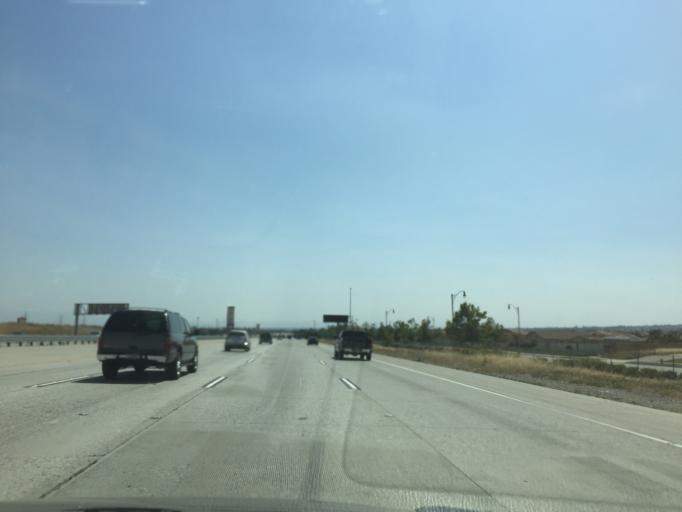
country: US
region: California
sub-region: San Bernardino County
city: Fontana
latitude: 34.1579
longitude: -117.4703
